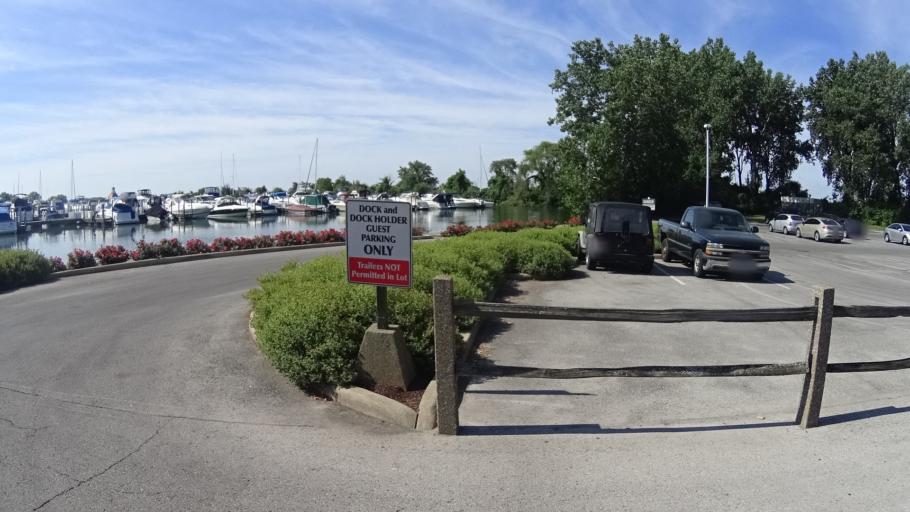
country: US
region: Ohio
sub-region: Erie County
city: Sandusky
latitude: 41.4813
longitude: -82.6875
